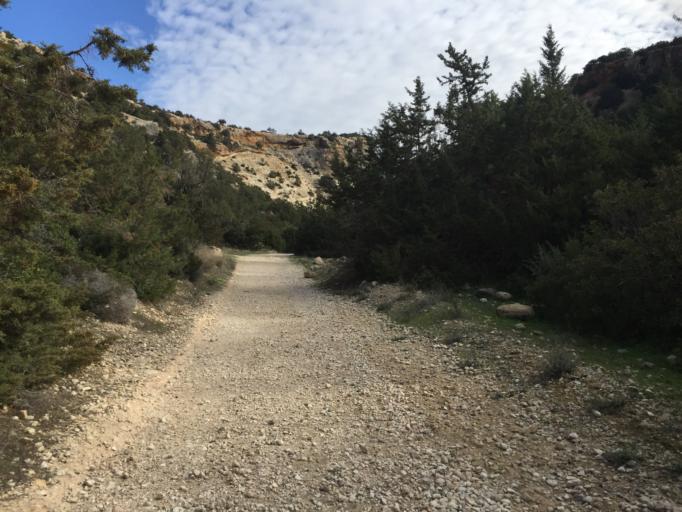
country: CY
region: Pafos
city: Pegeia
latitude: 34.9230
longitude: 32.3406
